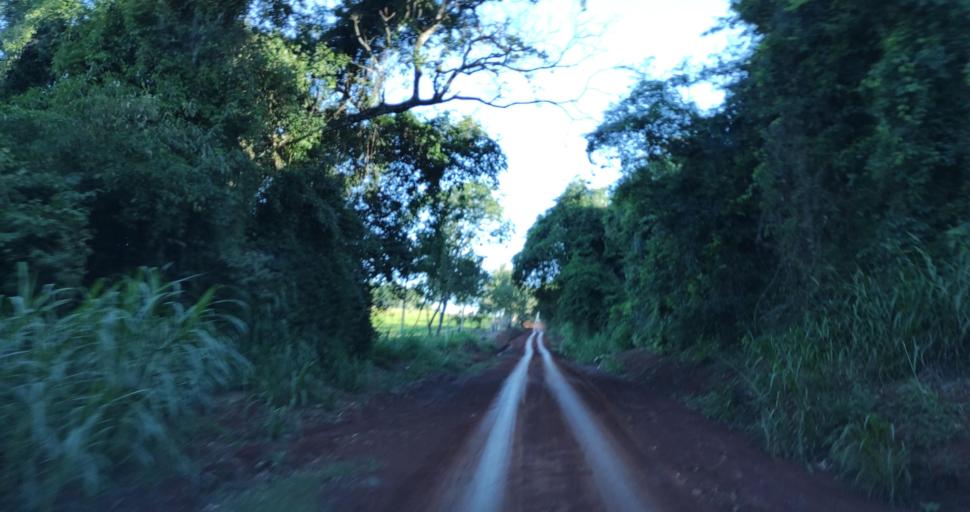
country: AR
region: Misiones
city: Puerto Rico
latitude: -26.8342
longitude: -55.0121
